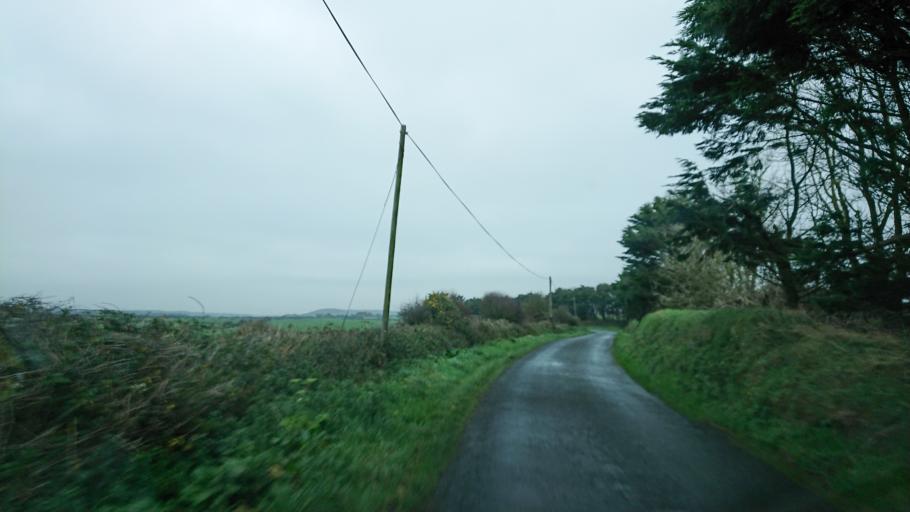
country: IE
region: Munster
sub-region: Waterford
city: Dunmore East
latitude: 52.1466
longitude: -7.0502
